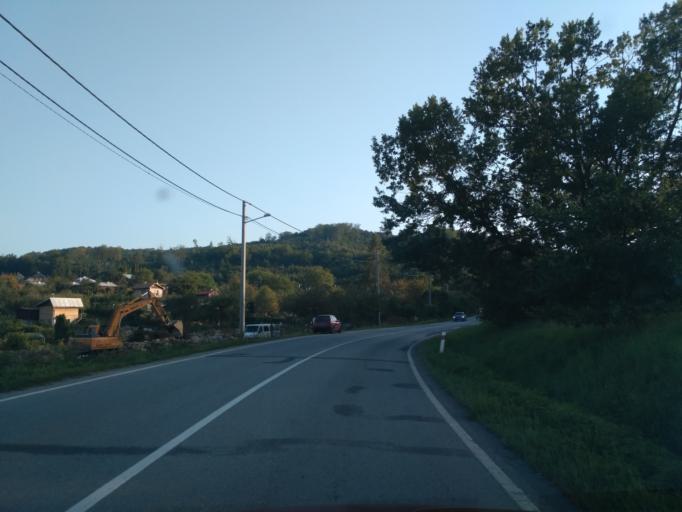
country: SK
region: Presovsky
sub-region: Okres Presov
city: Presov
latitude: 48.9950
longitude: 21.2021
